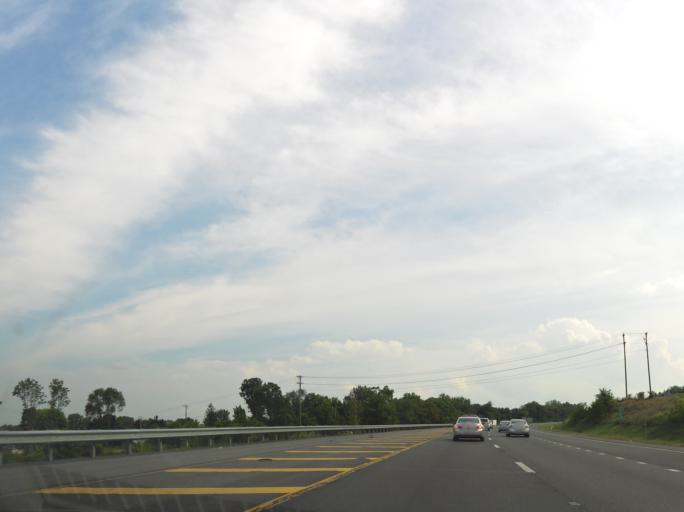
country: US
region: West Virginia
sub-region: Berkeley County
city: Martinsburg
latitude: 39.4399
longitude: -77.9895
